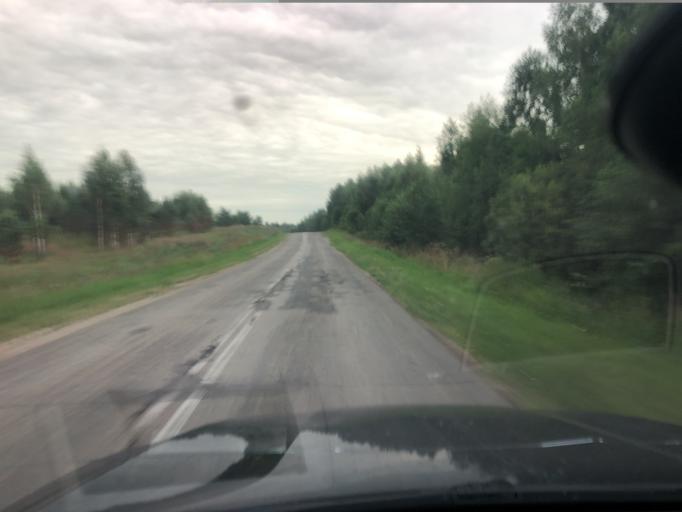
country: RU
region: Jaroslavl
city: Petrovsk
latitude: 57.0011
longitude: 39.0631
